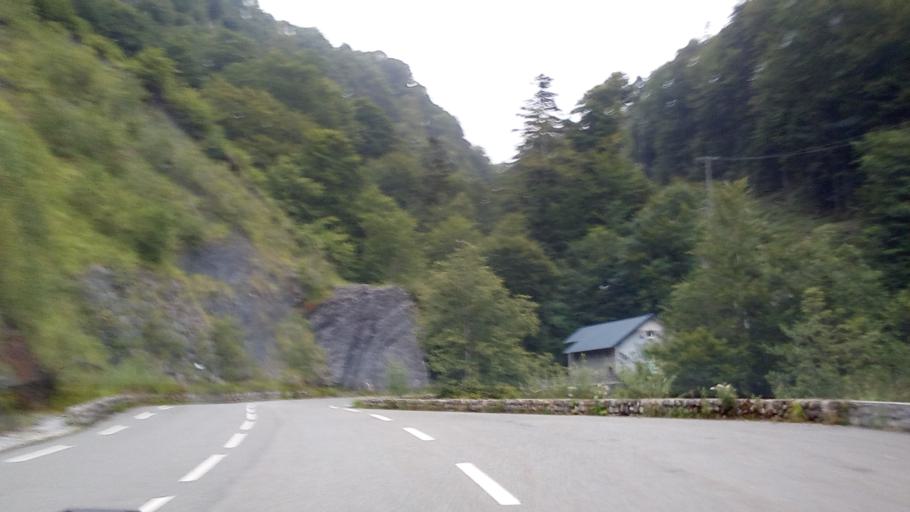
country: FR
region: Aquitaine
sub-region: Departement des Pyrenees-Atlantiques
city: Laruns
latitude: 42.9640
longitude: -0.3468
